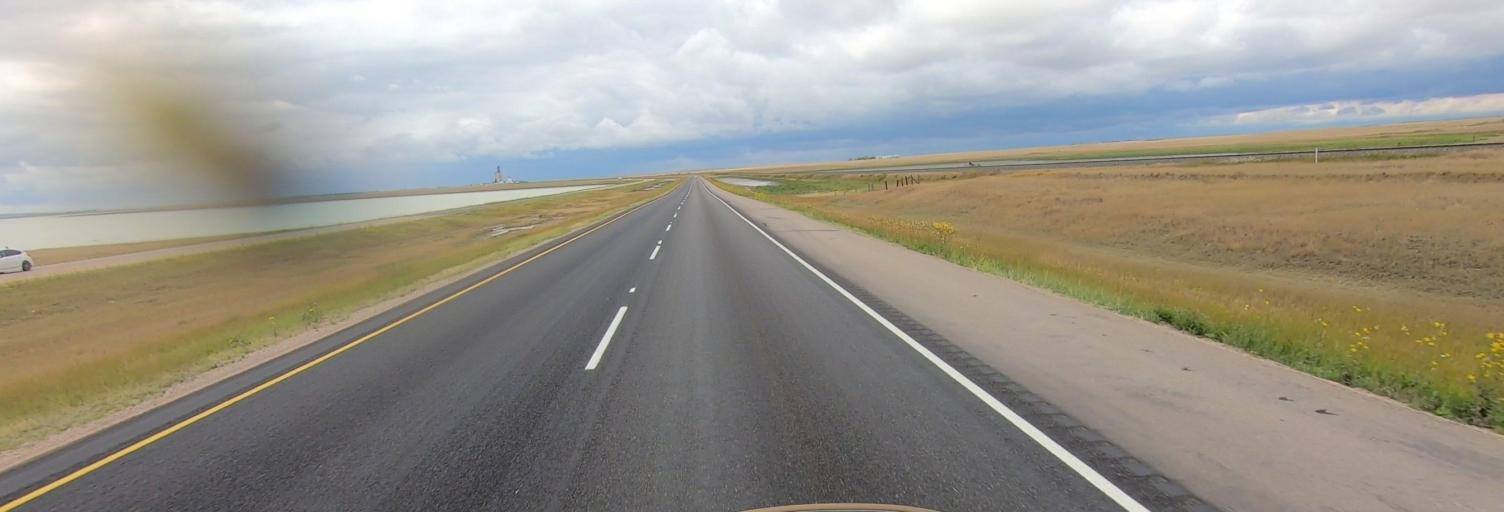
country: CA
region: Saskatchewan
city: Swift Current
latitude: 50.4192
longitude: -107.0937
